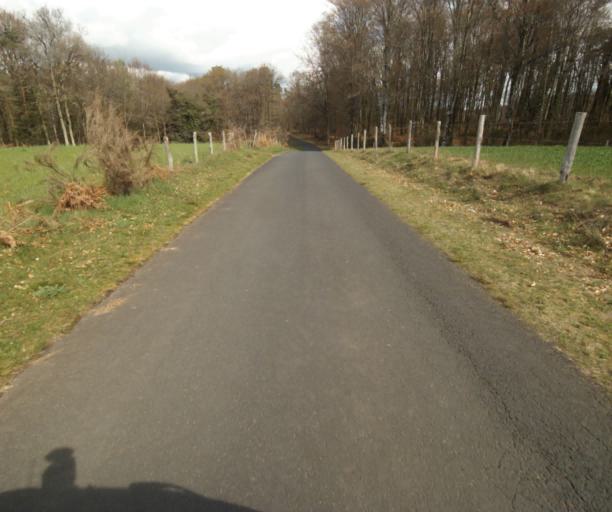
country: FR
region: Limousin
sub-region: Departement de la Correze
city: Correze
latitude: 45.3567
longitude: 1.8982
